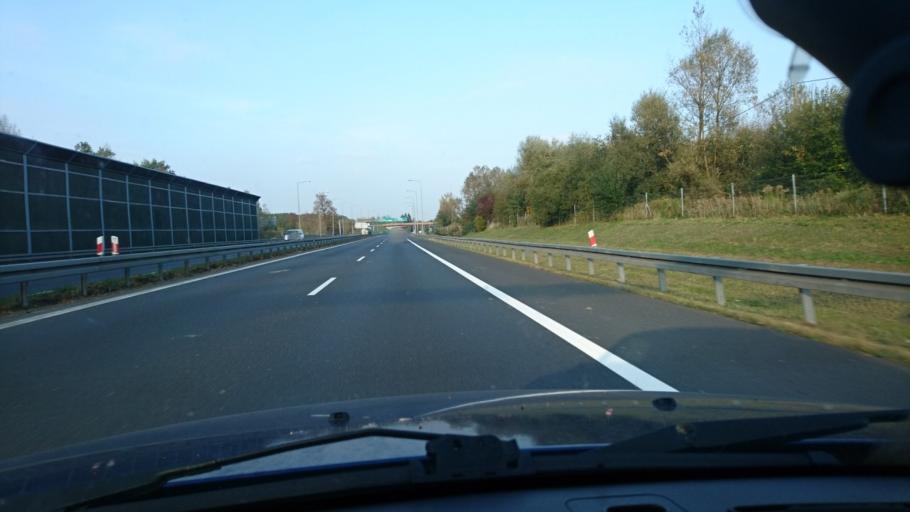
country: PL
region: Silesian Voivodeship
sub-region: Powiat bielski
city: Mazancowice
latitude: 49.8249
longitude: 18.9647
